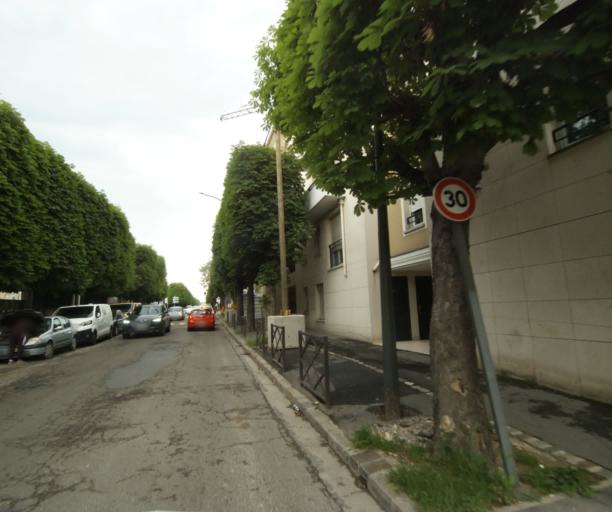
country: FR
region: Ile-de-France
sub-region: Departement du Val-d'Oise
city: Argenteuil
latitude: 48.9422
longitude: 2.2424
